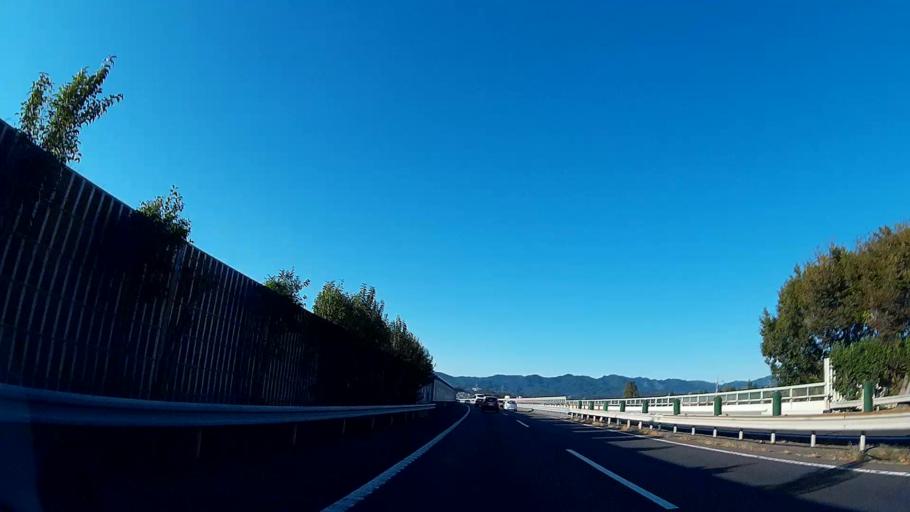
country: JP
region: Tokyo
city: Hachioji
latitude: 35.6748
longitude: 139.3118
